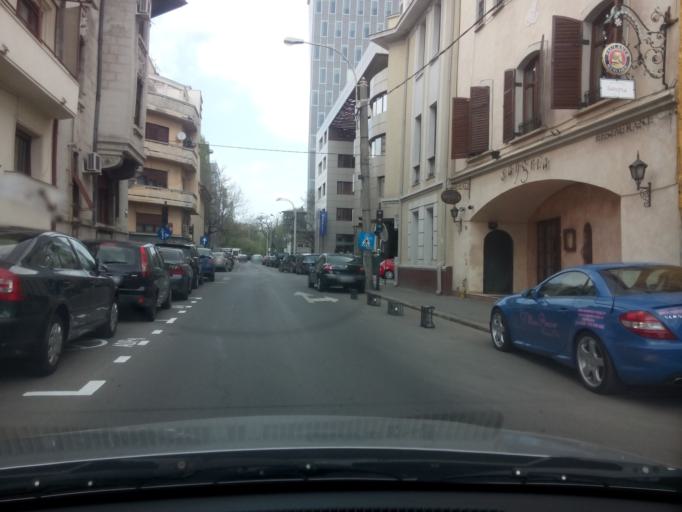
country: RO
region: Bucuresti
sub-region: Municipiul Bucuresti
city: Bucharest
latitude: 44.4515
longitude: 26.0956
